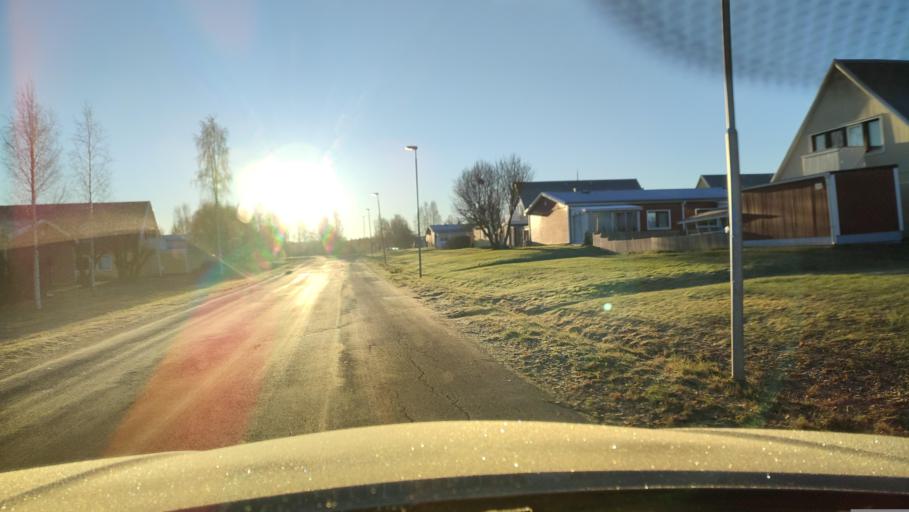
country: SE
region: Vaesterbotten
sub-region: Skelleftea Kommun
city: Skelleftea
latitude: 64.7434
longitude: 20.9832
